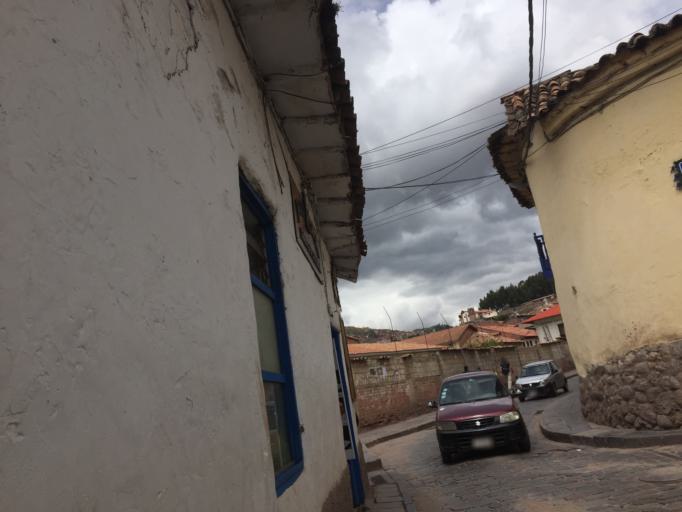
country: PE
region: Cusco
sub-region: Provincia de Cusco
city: Cusco
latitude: -13.5167
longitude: -71.9746
